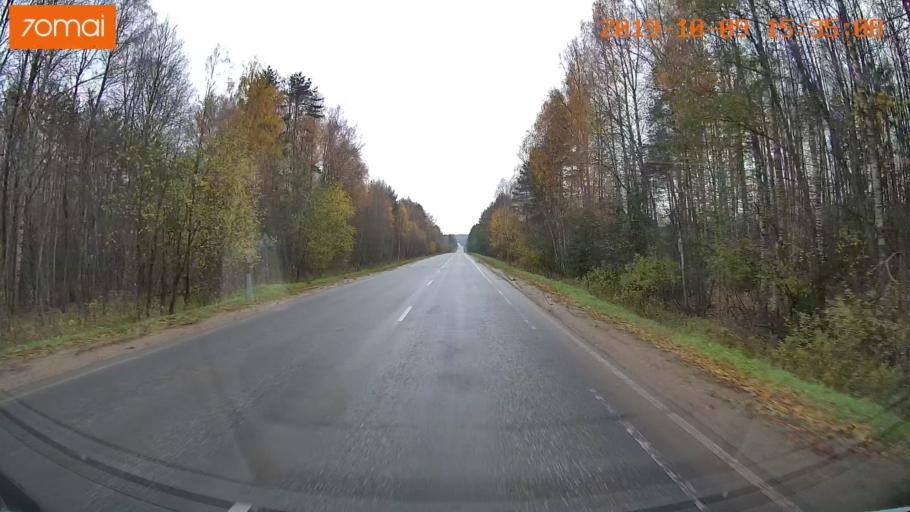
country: RU
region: Kostroma
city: Oktyabr'skiy
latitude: 57.9351
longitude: 41.2333
